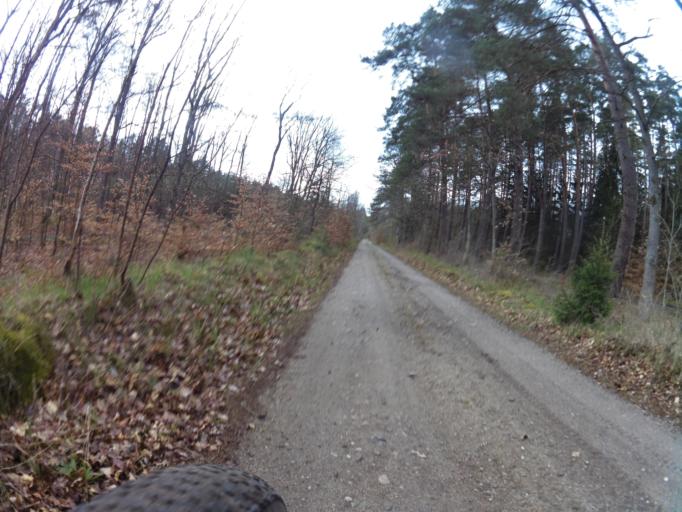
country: PL
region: West Pomeranian Voivodeship
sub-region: Powiat slawienski
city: Slawno
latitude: 54.3209
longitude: 16.7724
